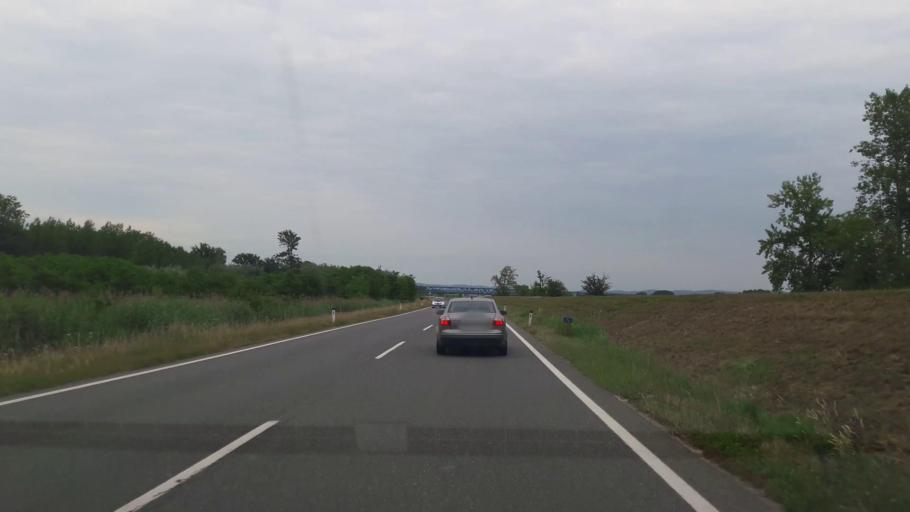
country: AT
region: Lower Austria
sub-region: Politischer Bezirk Tulln
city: Tulln
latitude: 48.3372
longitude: 16.0421
